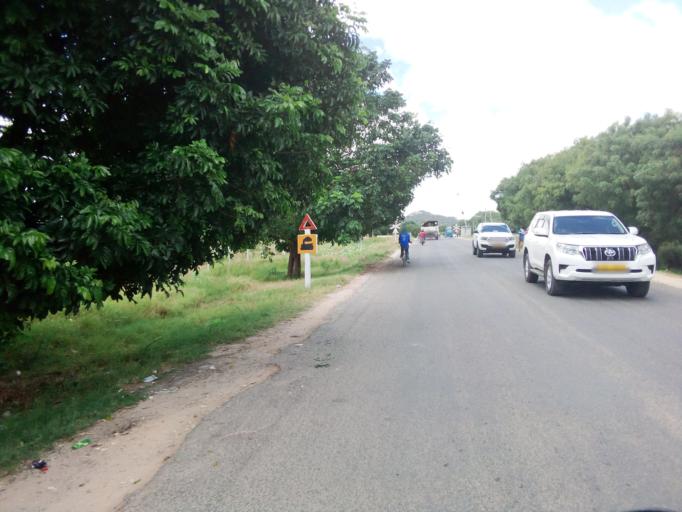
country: TZ
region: Dodoma
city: Dodoma
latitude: -6.1845
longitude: 35.7587
